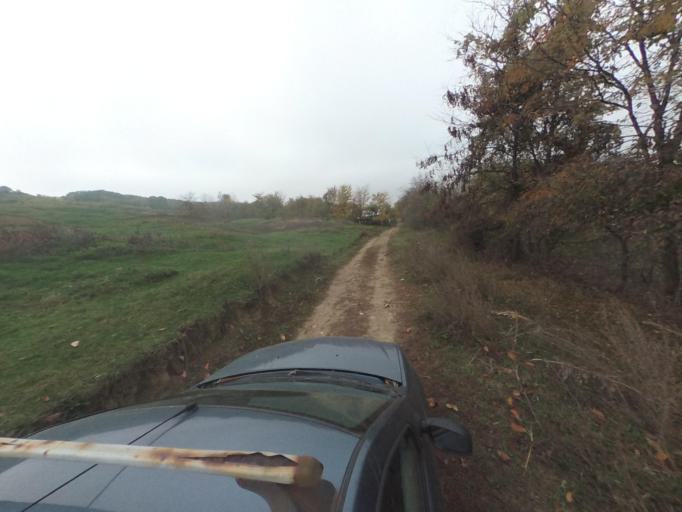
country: RO
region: Vaslui
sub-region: Comuna Bacesti
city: Bacesti
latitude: 46.8322
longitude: 27.2319
